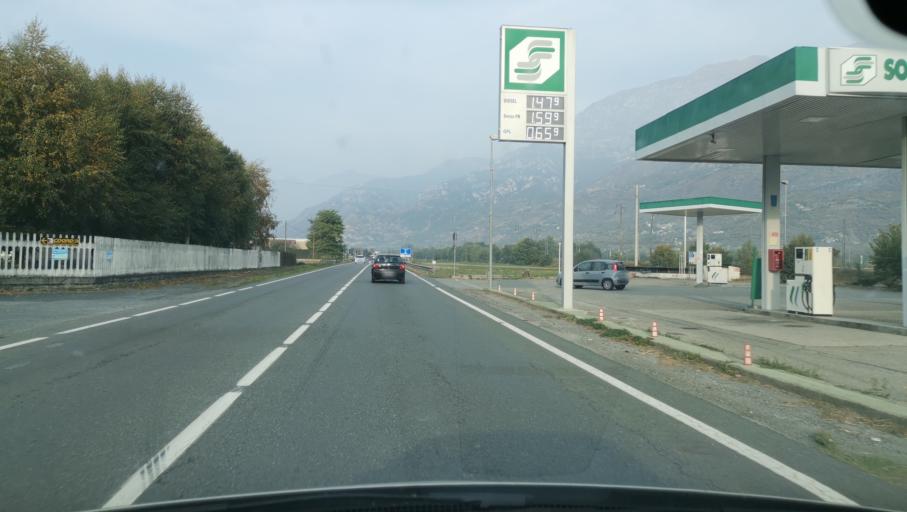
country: IT
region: Piedmont
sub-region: Provincia di Torino
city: Bruzolo
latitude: 45.1313
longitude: 7.1975
